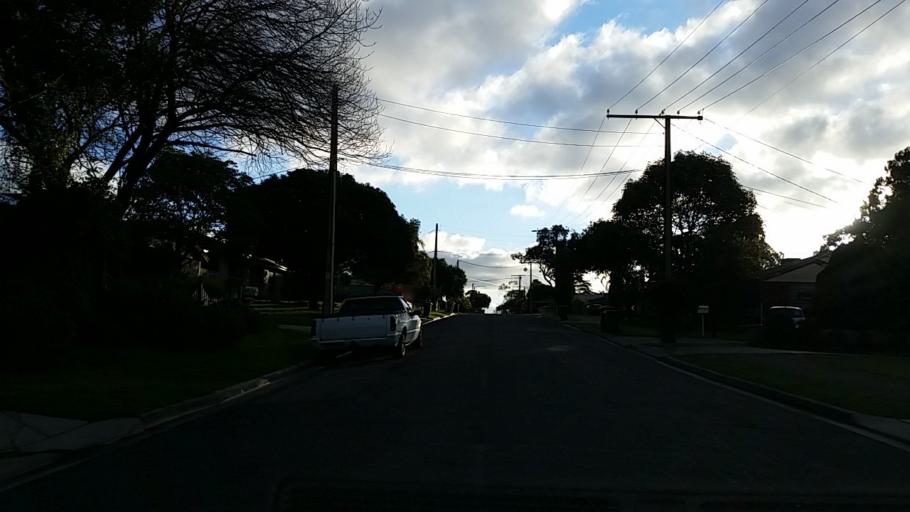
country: AU
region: South Australia
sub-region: Tea Tree Gully
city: Hope Valley
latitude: -34.8467
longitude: 138.7068
